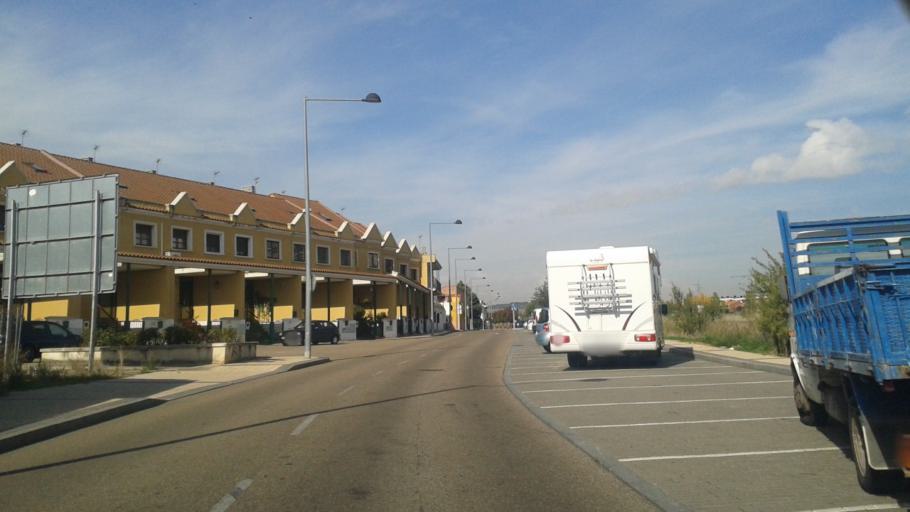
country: ES
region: Castille and Leon
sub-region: Provincia de Valladolid
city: Arroyo
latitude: 41.6292
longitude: -4.7710
